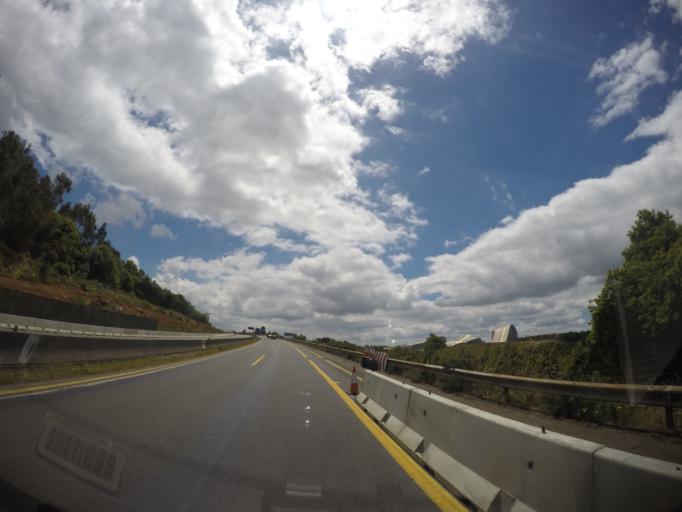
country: ES
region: Galicia
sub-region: Provincia da Coruna
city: Negreira
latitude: 42.8369
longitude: -8.7209
